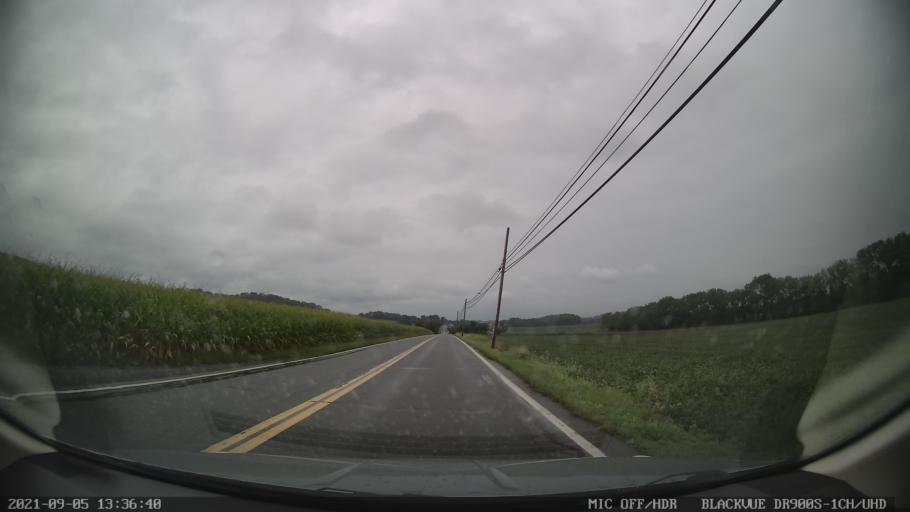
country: US
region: Pennsylvania
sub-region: Lehigh County
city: Breinigsville
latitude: 40.5792
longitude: -75.6523
